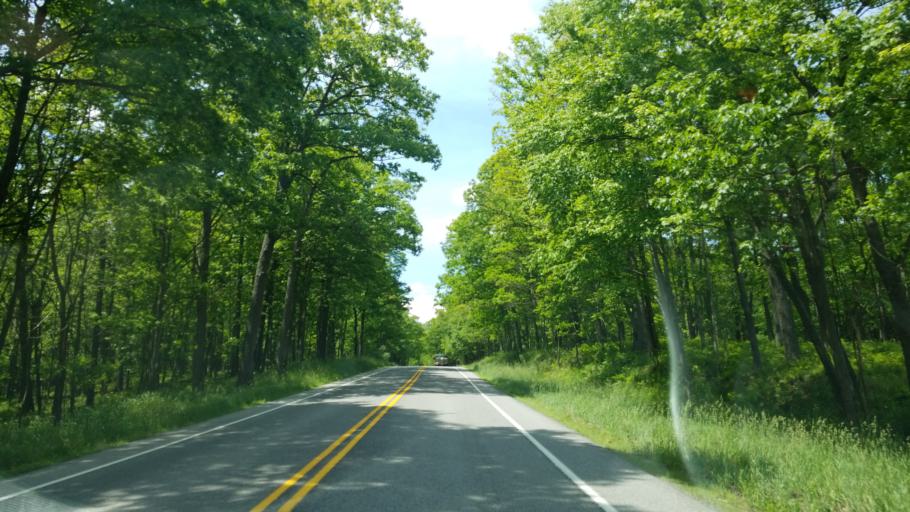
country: US
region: Pennsylvania
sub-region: Blair County
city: Tipton
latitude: 40.7179
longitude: -78.3255
